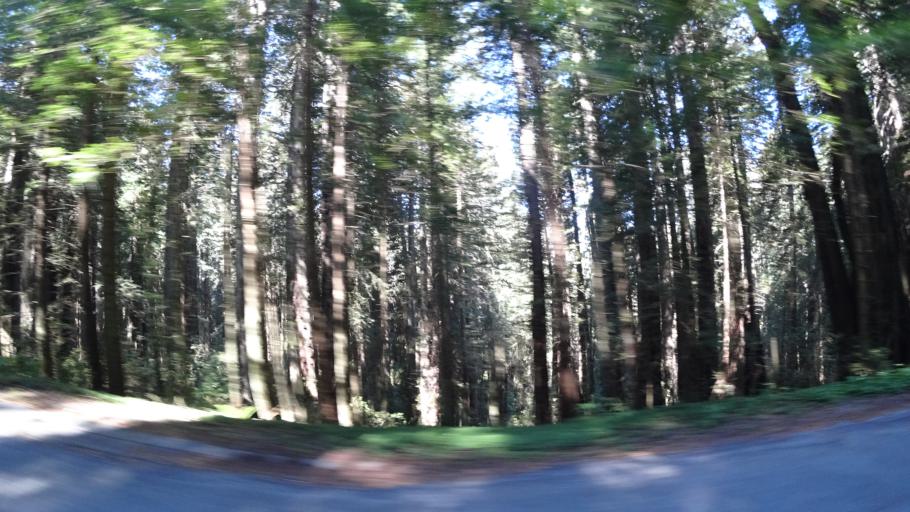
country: US
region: California
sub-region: Del Norte County
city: Bertsch-Oceanview
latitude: 41.6566
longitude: -124.1154
